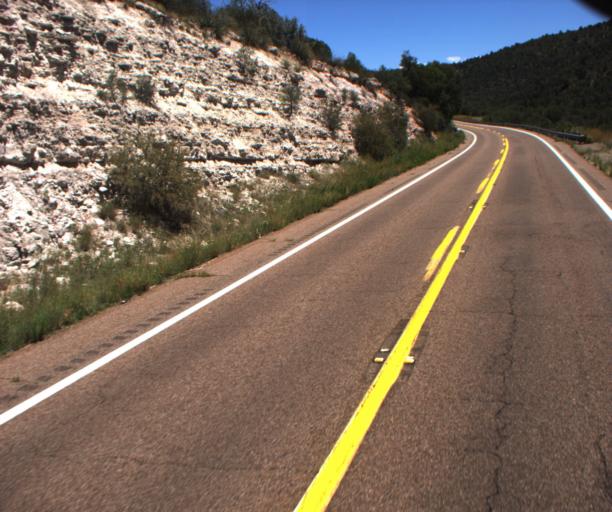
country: US
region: Arizona
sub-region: Navajo County
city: Cibecue
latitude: 33.8385
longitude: -110.4352
